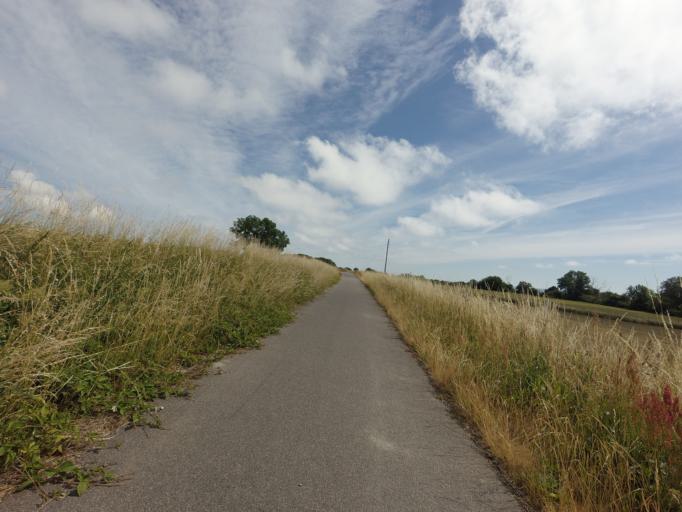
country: SE
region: Skane
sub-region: Simrishamns Kommun
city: Simrishamn
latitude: 55.5052
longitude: 14.3311
